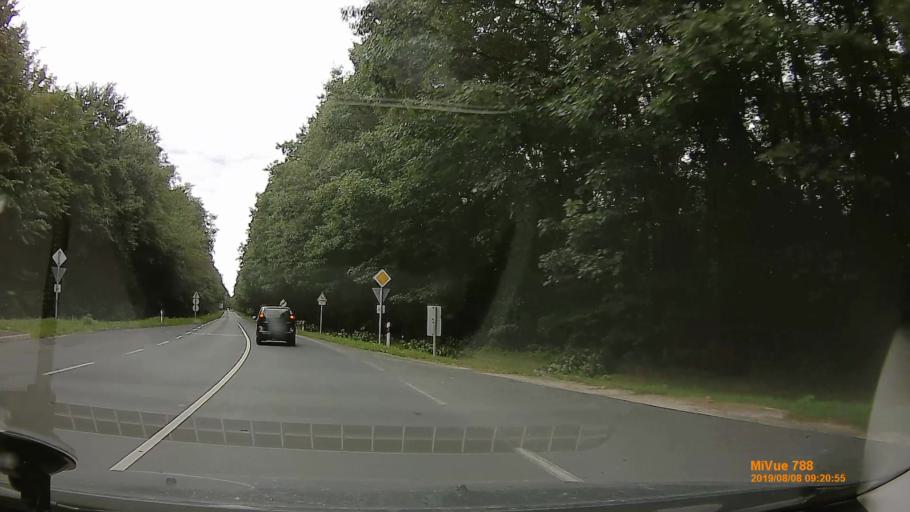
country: HU
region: Zala
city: Zalaegerszeg
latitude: 46.8766
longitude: 16.8533
